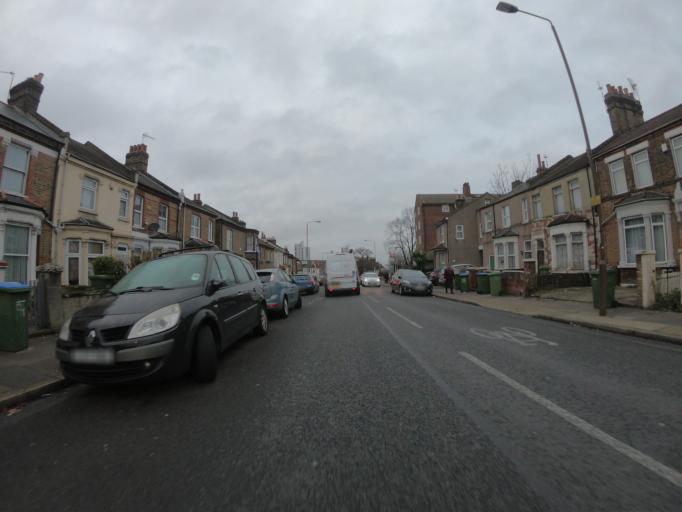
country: GB
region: England
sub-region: Greater London
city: Woolwich
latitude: 51.4832
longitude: 0.0829
